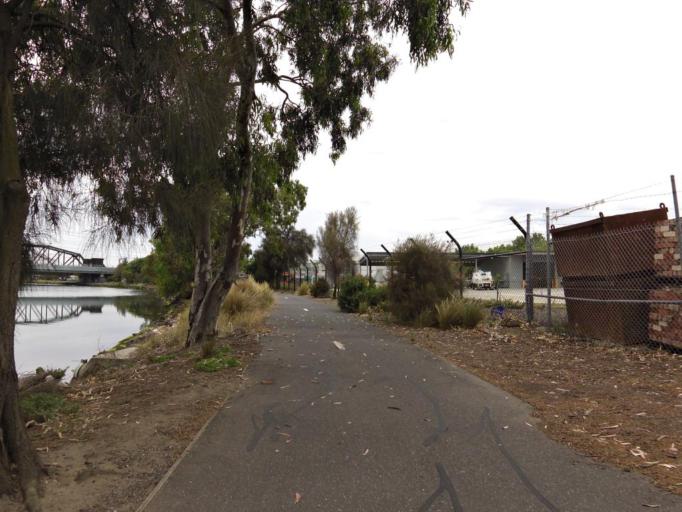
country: AU
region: Victoria
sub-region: Maribyrnong
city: Footscray
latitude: -37.8004
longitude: 144.9154
